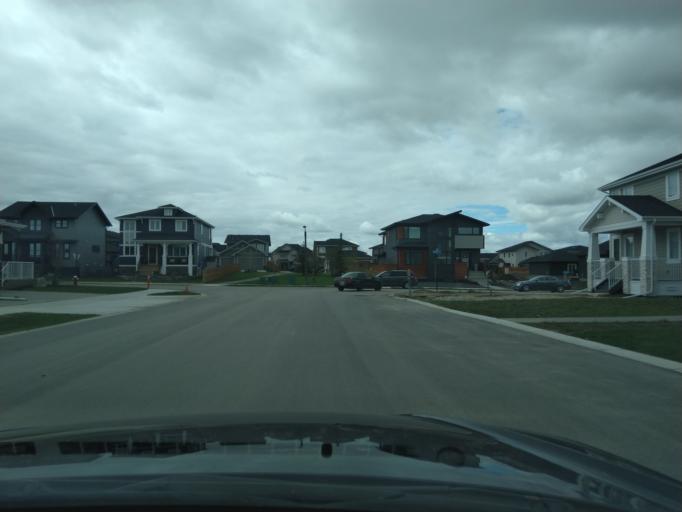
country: CA
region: Alberta
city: Cochrane
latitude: 51.1095
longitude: -114.3935
